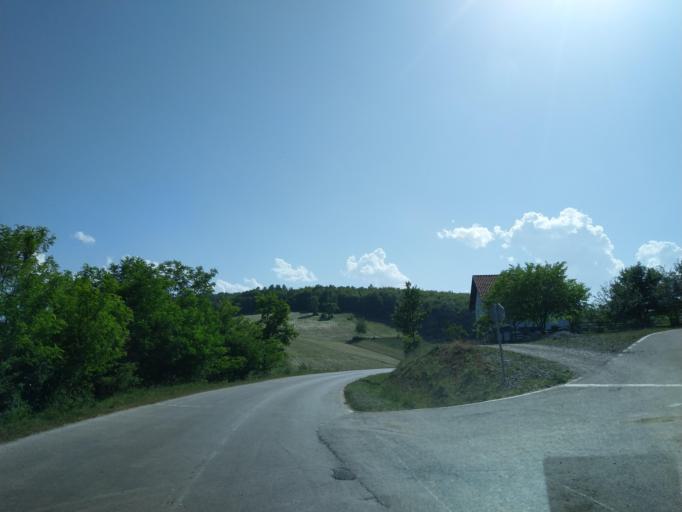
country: RS
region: Central Serbia
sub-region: Zlatiborski Okrug
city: Uzice
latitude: 43.8794
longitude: 19.7535
